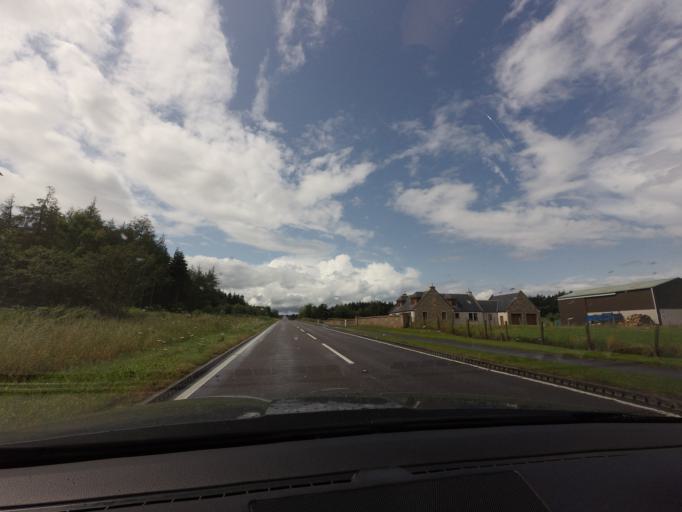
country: GB
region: Scotland
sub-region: Moray
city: Lhanbryd
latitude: 57.6269
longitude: -3.1593
